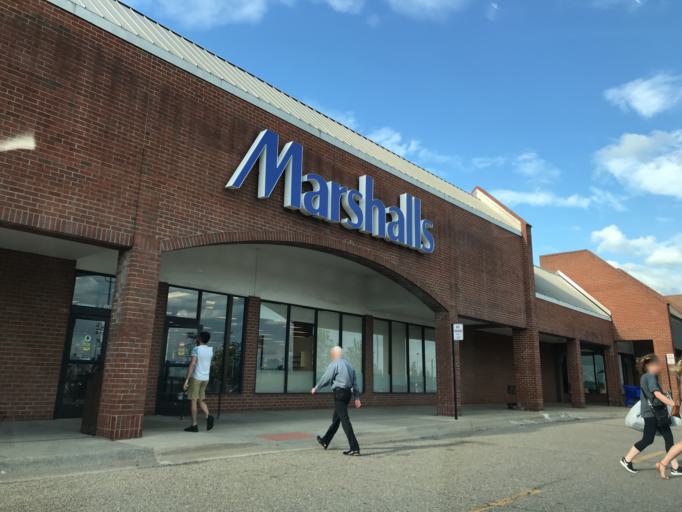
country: US
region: Michigan
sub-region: Oakland County
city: Novi
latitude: 42.4945
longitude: -83.4799
